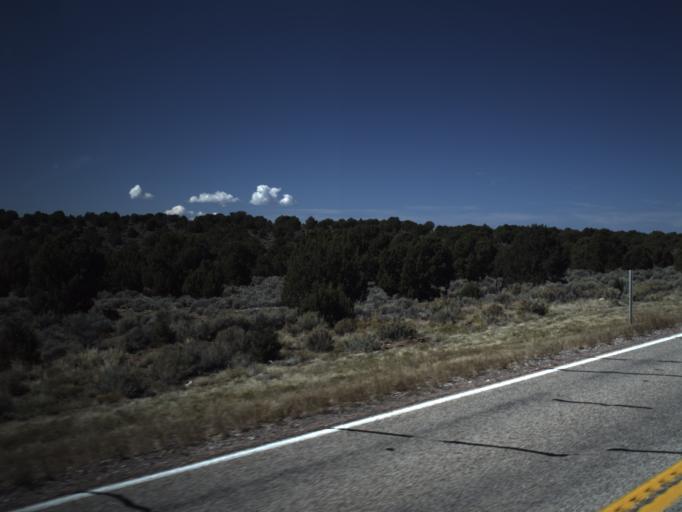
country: US
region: Utah
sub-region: Washington County
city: Enterprise
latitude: 37.6623
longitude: -113.4644
